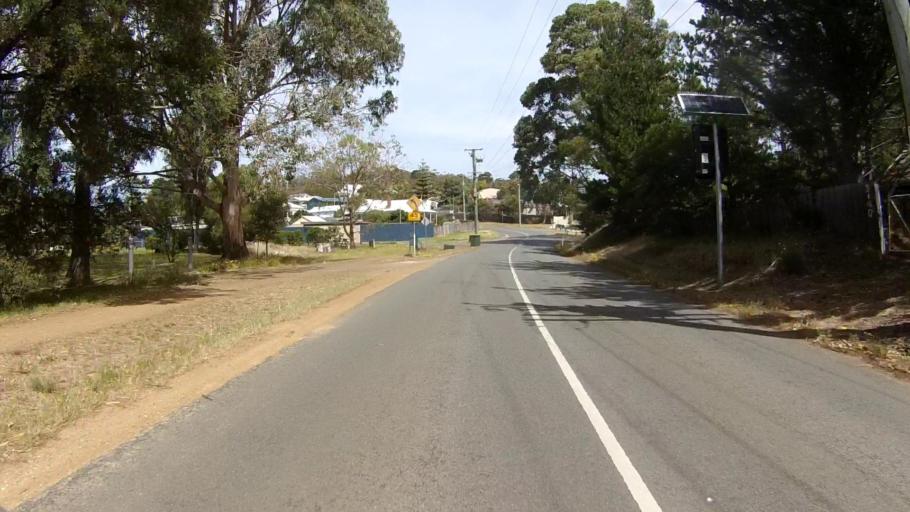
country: AU
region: Tasmania
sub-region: Kingborough
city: Blackmans Bay
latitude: -43.0264
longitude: 147.4170
